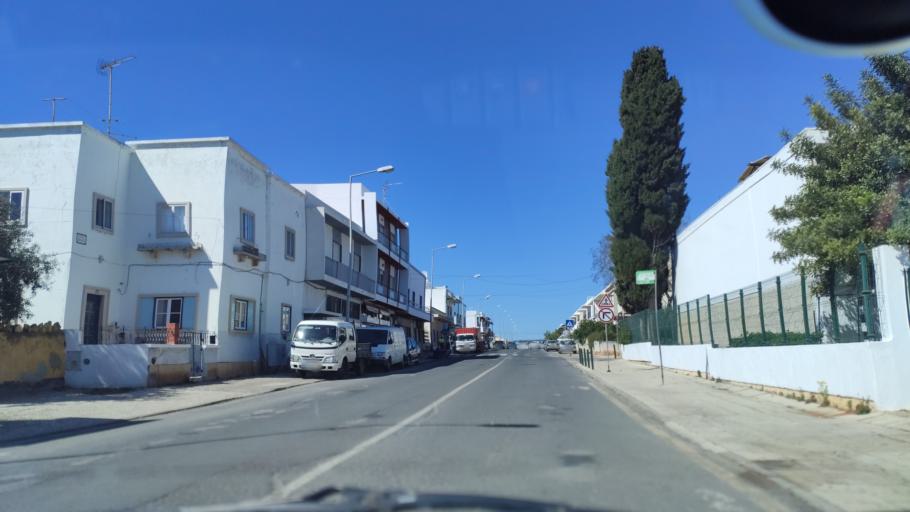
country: PT
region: Faro
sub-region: Olhao
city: Olhao
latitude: 37.0348
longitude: -7.8474
